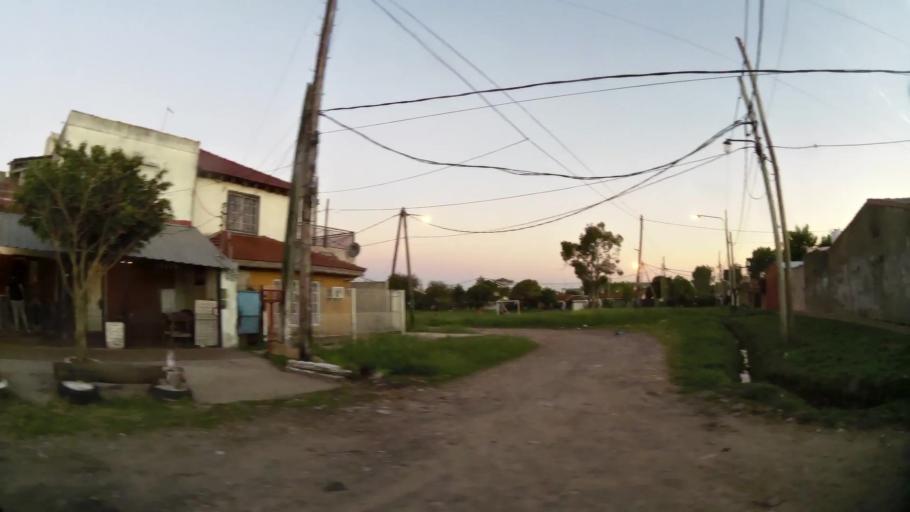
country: AR
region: Buenos Aires
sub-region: Partido de Almirante Brown
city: Adrogue
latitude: -34.7933
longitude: -58.3223
